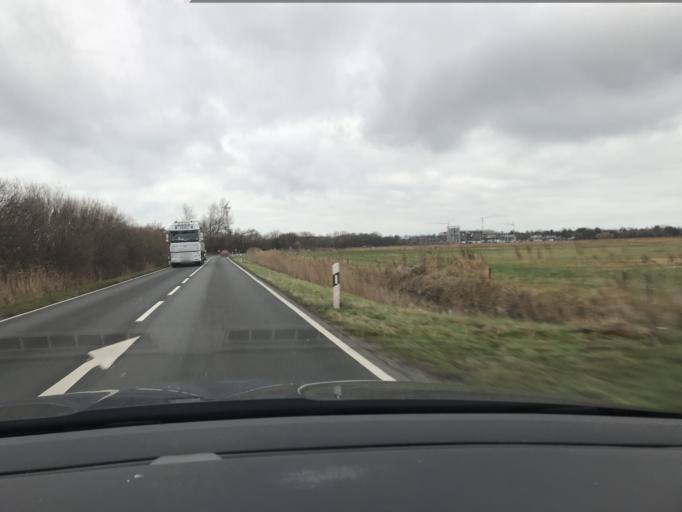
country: DE
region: Mecklenburg-Vorpommern
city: Ostseebad Dierhagen
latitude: 54.3412
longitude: 12.3811
